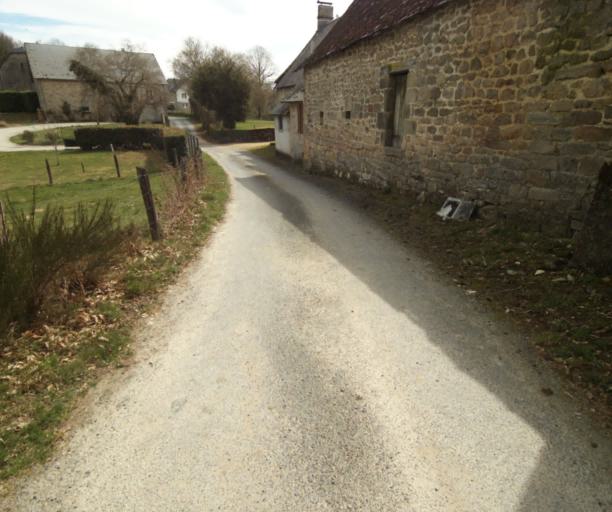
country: FR
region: Limousin
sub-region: Departement de la Correze
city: Correze
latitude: 45.3882
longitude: 1.9608
